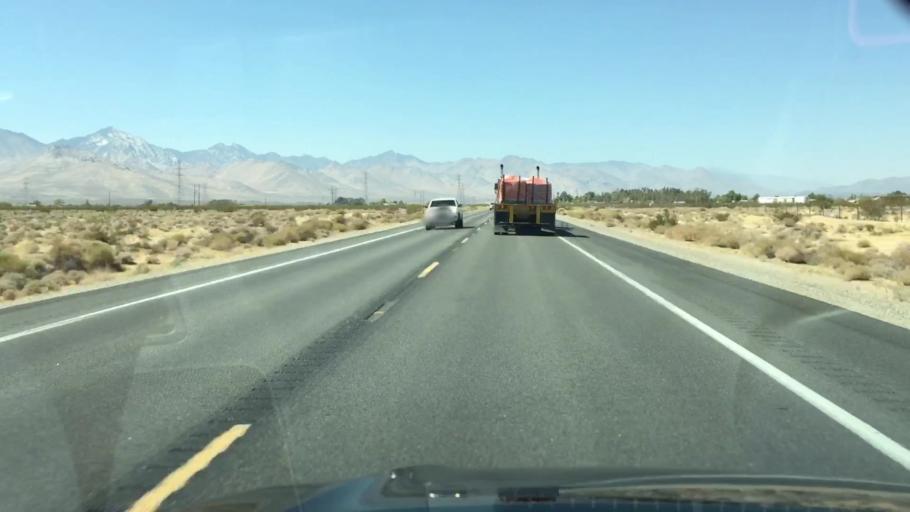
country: US
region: California
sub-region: Kern County
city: China Lake Acres
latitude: 35.6310
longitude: -117.7829
